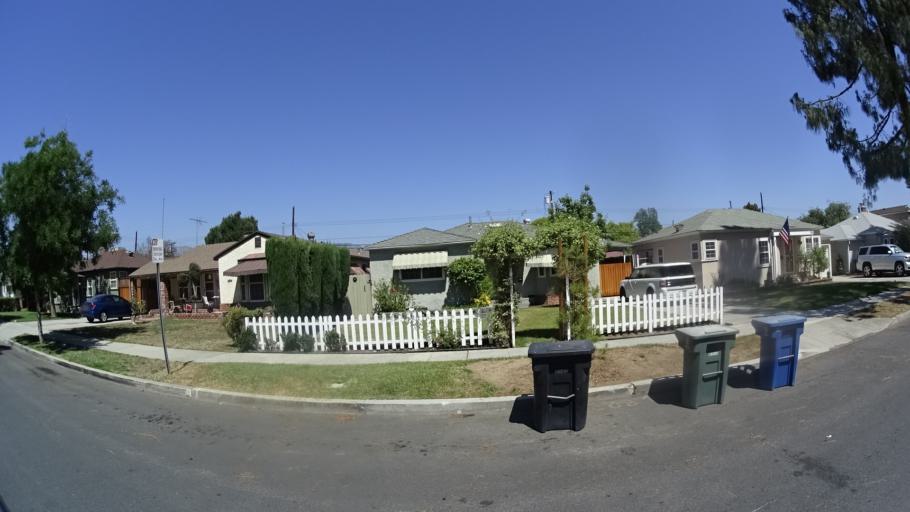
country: US
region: California
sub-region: Los Angeles County
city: North Hollywood
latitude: 34.1838
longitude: -118.3545
